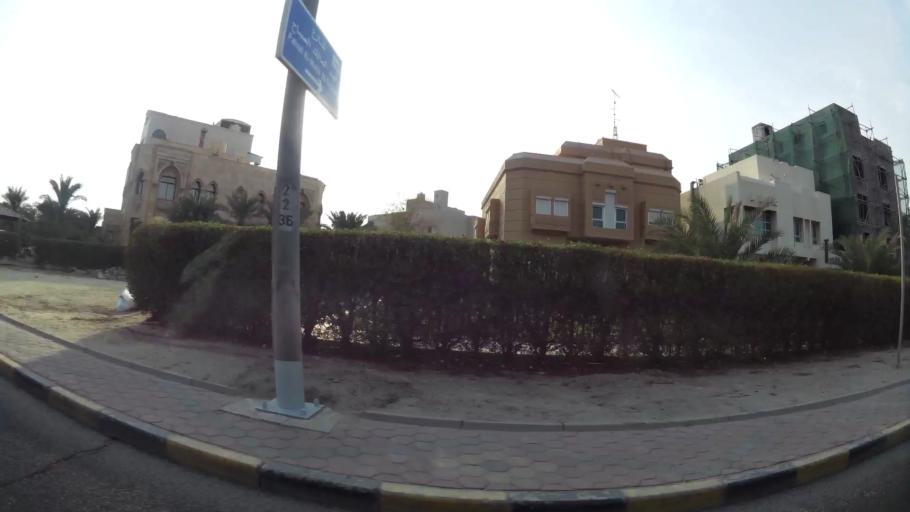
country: KW
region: Mubarak al Kabir
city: Mubarak al Kabir
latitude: 29.2096
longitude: 48.0685
